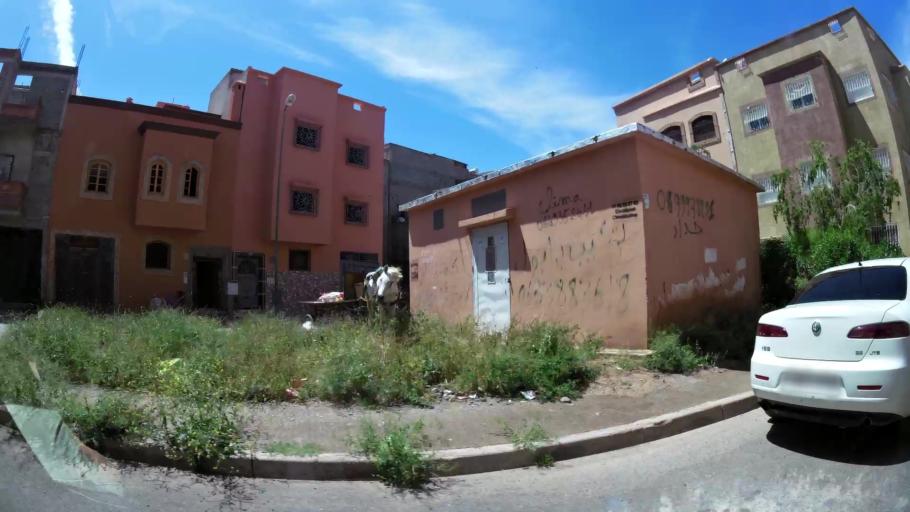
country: MA
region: Marrakech-Tensift-Al Haouz
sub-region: Marrakech
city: Marrakesh
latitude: 31.6407
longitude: -8.0497
